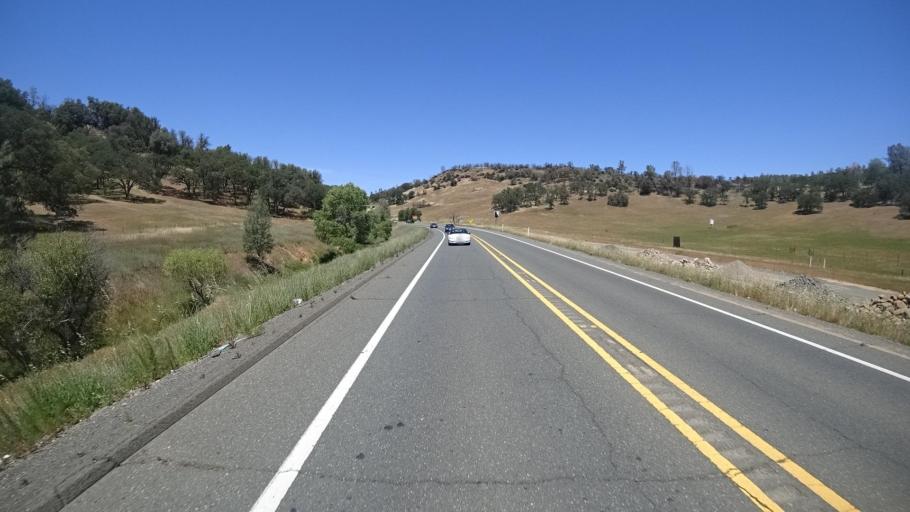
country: US
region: California
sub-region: Lake County
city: Hidden Valley Lake
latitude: 38.8243
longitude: -122.5797
